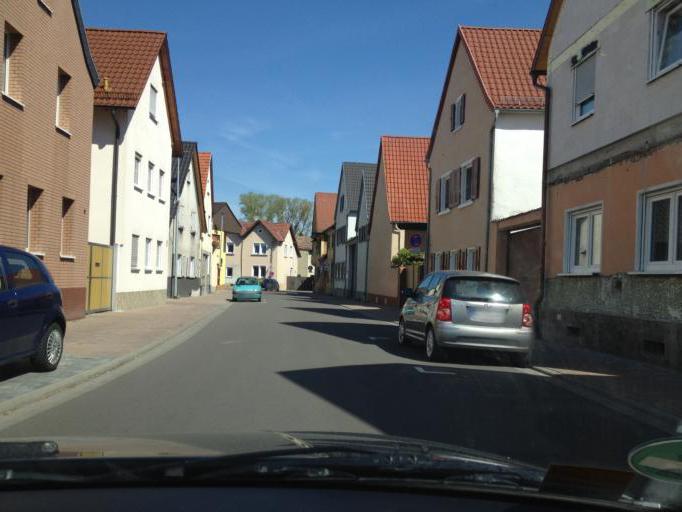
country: DE
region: Rheinland-Pfalz
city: Waldsee
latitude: 49.3955
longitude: 8.4415
